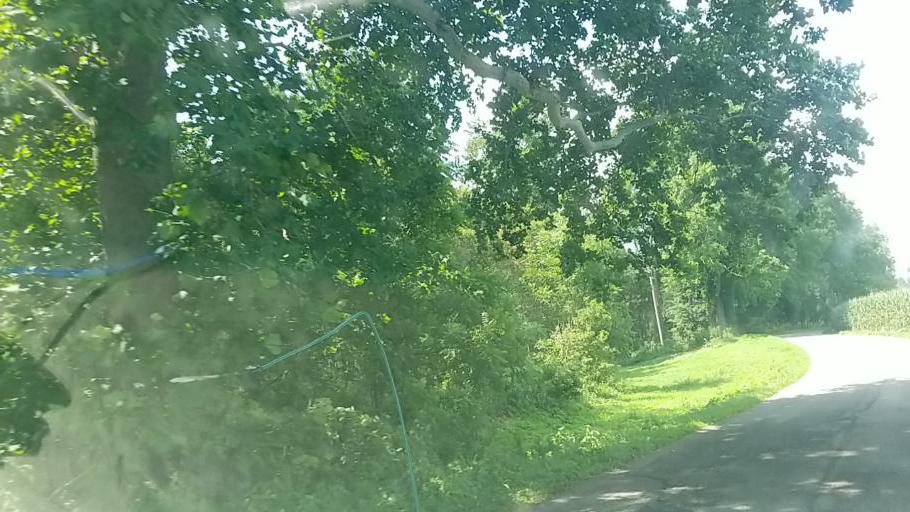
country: US
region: Ohio
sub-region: Sandusky County
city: Bellville
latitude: 40.5995
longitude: -82.4093
